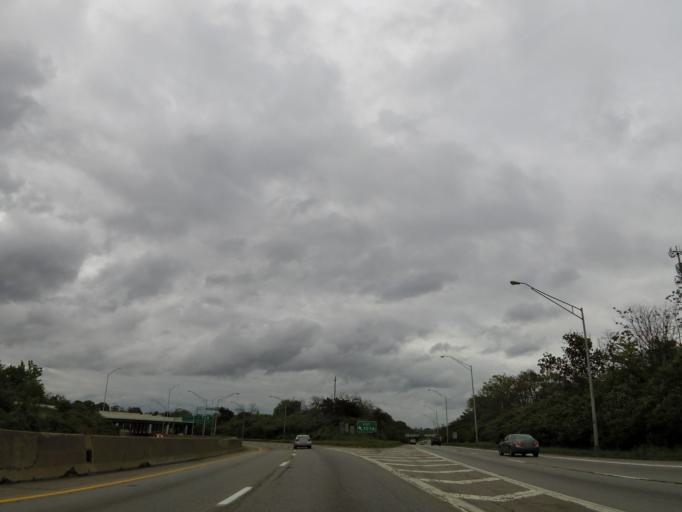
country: US
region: Ohio
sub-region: Franklin County
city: Columbus
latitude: 39.9543
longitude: -82.9860
